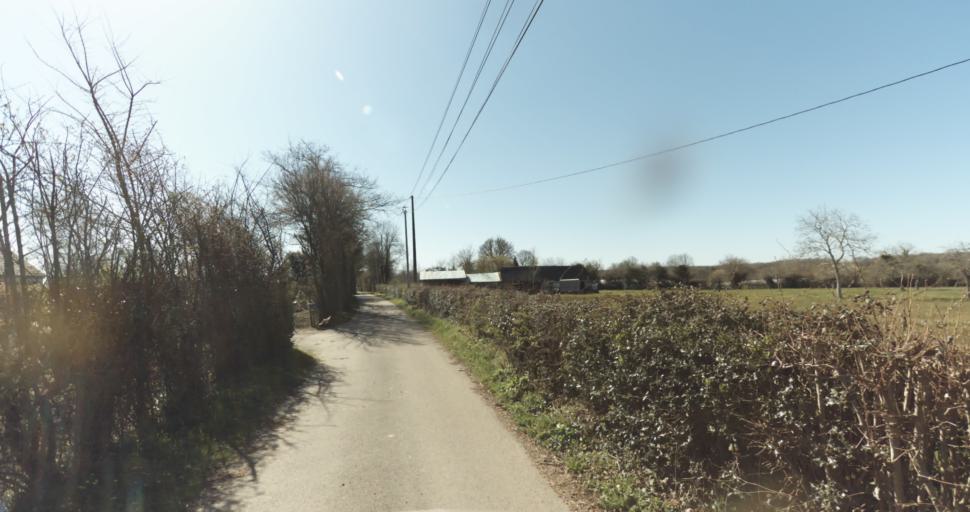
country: FR
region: Lower Normandy
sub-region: Departement du Calvados
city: Livarot
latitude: 48.9890
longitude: 0.1025
